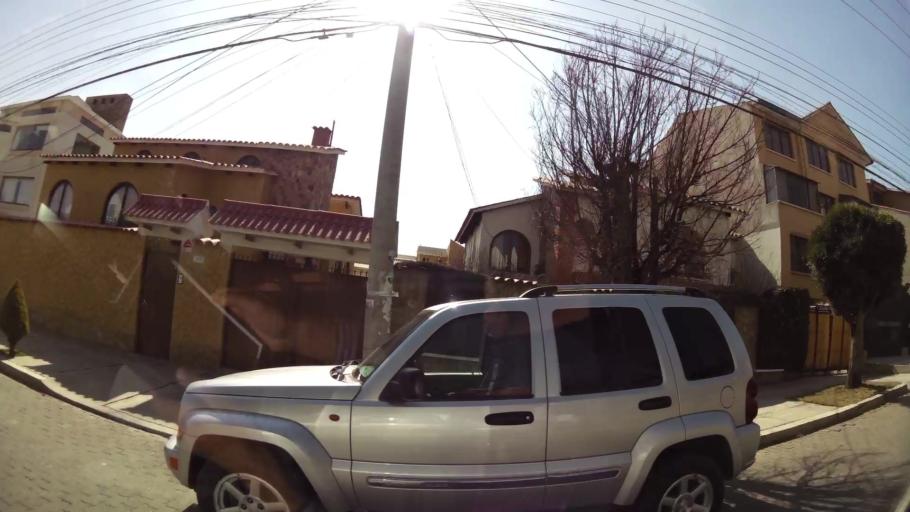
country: BO
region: La Paz
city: La Paz
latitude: -16.5339
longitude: -68.0716
